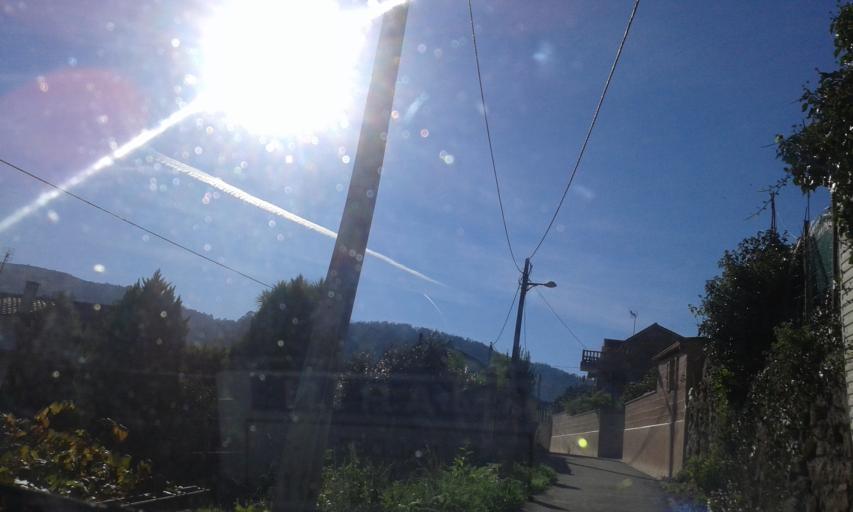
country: ES
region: Galicia
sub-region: Provincia de Pontevedra
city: Marin
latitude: 42.3598
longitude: -8.7424
